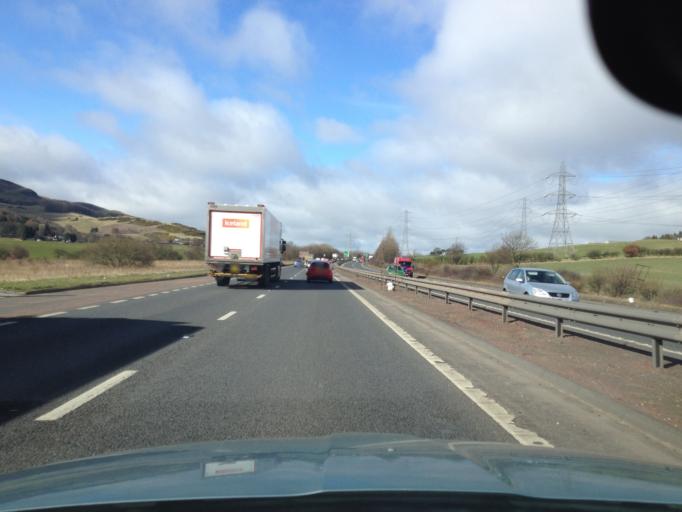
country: GB
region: Scotland
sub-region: Midlothian
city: Loanhead
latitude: 55.8919
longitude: -3.1846
